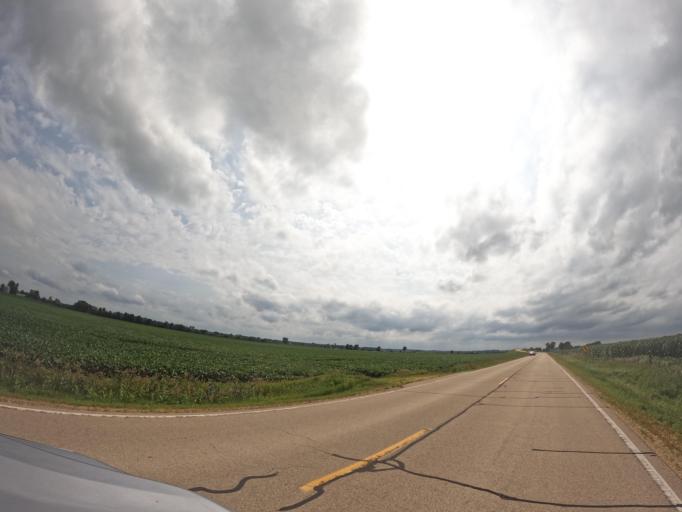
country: US
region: Iowa
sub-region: Clinton County
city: De Witt
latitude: 41.7859
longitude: -90.5604
